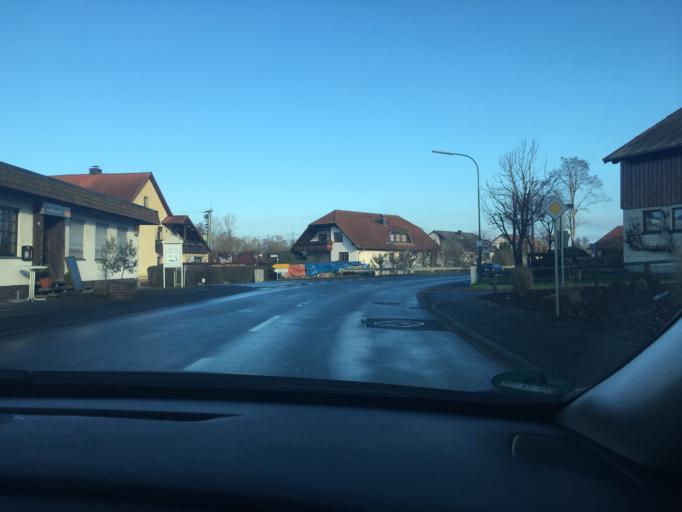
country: DE
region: Hesse
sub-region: Regierungsbezirk Kassel
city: Dipperz
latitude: 50.5676
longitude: 9.7611
